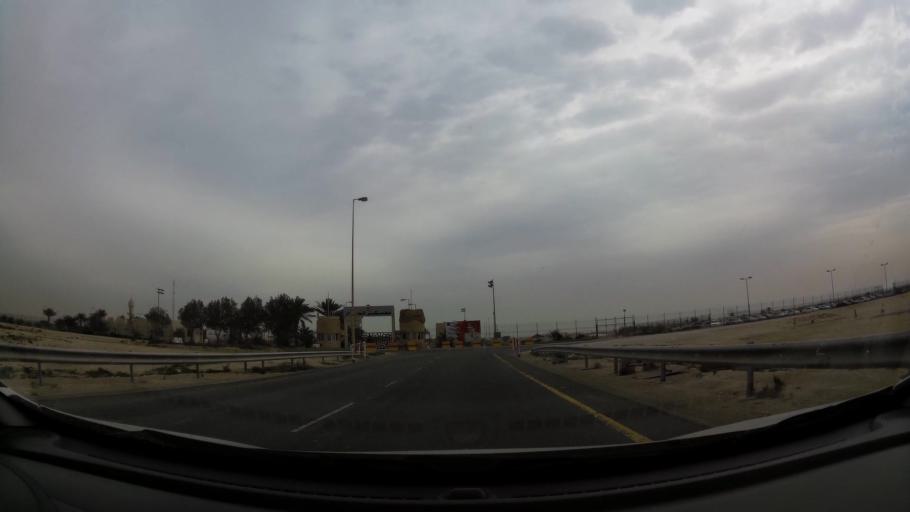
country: BH
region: Central Governorate
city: Dar Kulayb
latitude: 25.8869
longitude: 50.5796
